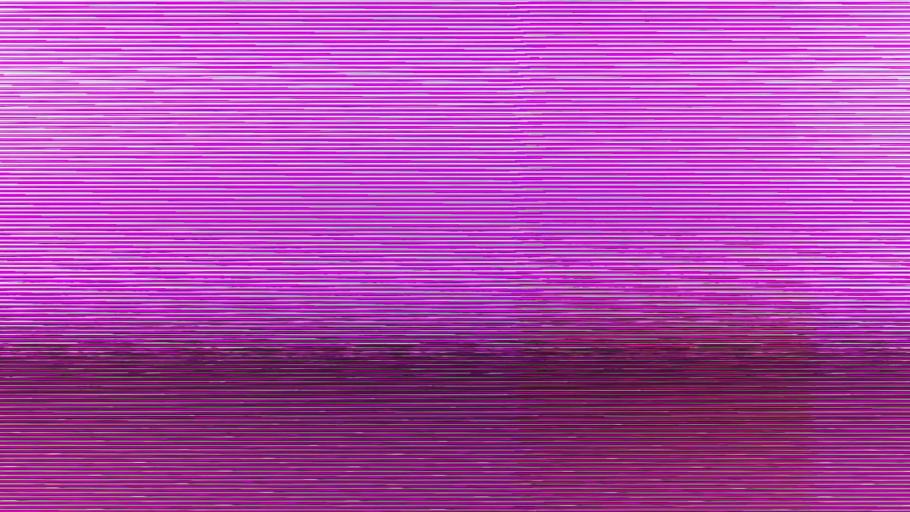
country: US
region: Michigan
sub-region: Macomb County
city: Romeo
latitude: 42.7611
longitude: -83.0102
